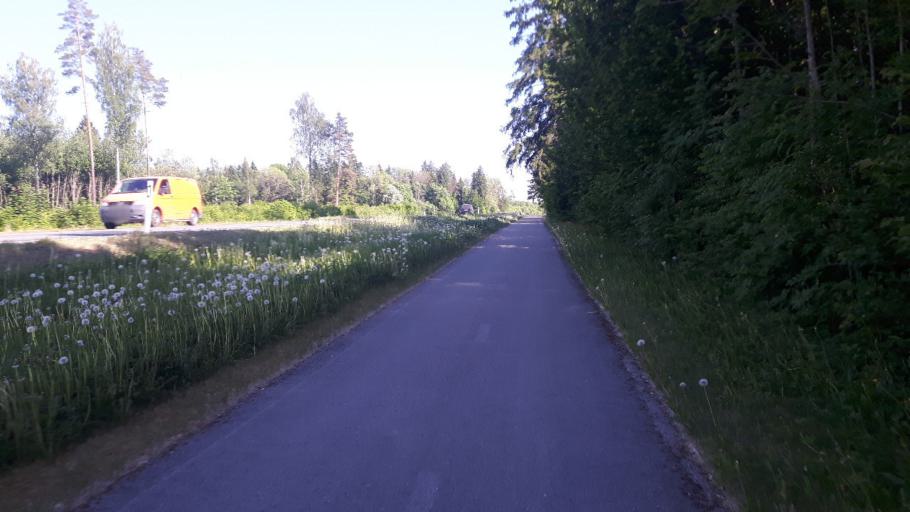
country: EE
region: Raplamaa
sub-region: Kehtna vald
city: Kehtna
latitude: 58.9555
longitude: 24.8691
